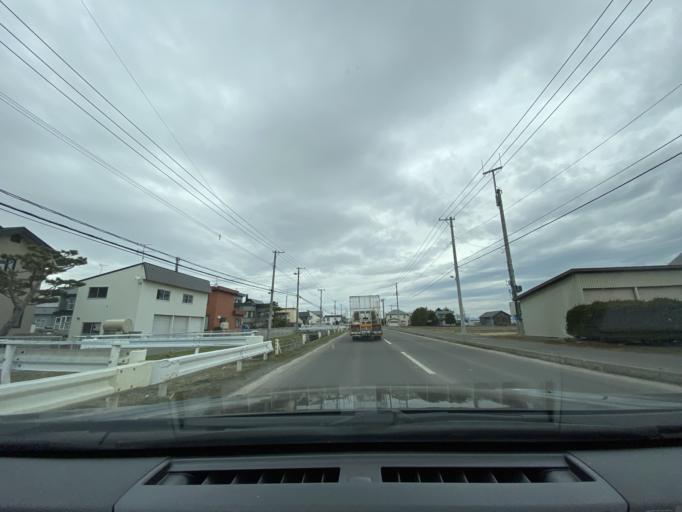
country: JP
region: Hokkaido
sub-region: Asahikawa-shi
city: Asahikawa
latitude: 43.7847
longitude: 142.4164
